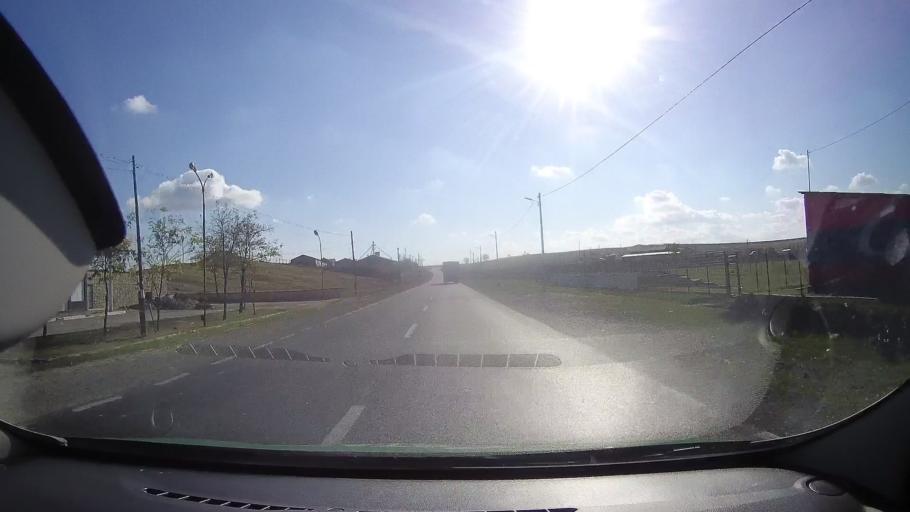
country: RO
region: Tulcea
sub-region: Comuna Baia
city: Baia
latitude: 44.7196
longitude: 28.6799
